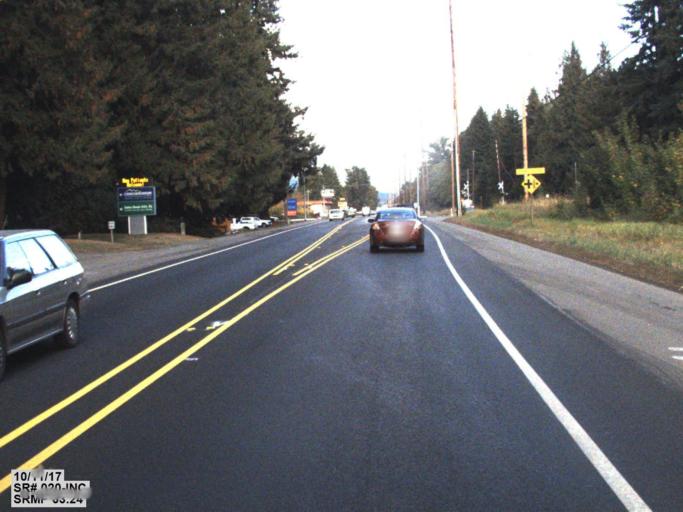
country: US
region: Washington
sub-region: Skagit County
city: Sedro-Woolley
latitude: 48.4939
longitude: -122.2768
